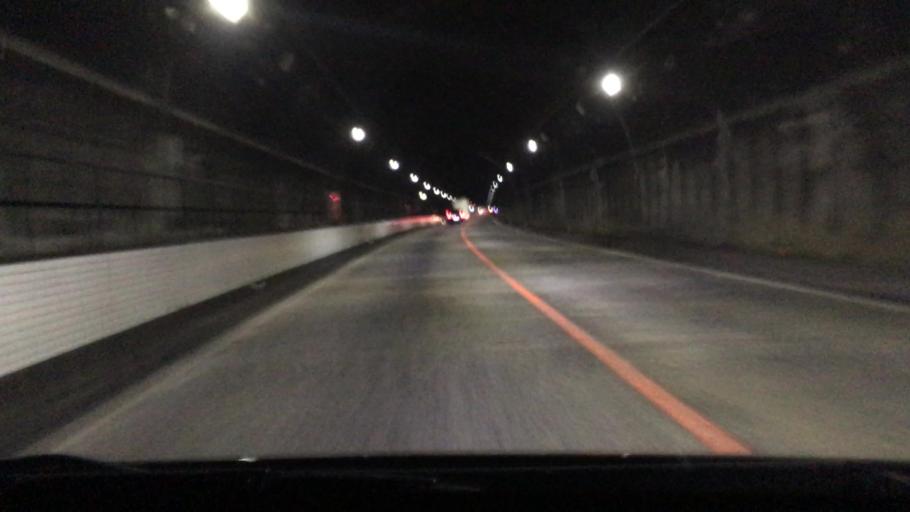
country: JP
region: Yamaguchi
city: Otake
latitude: 34.2174
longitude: 132.1957
